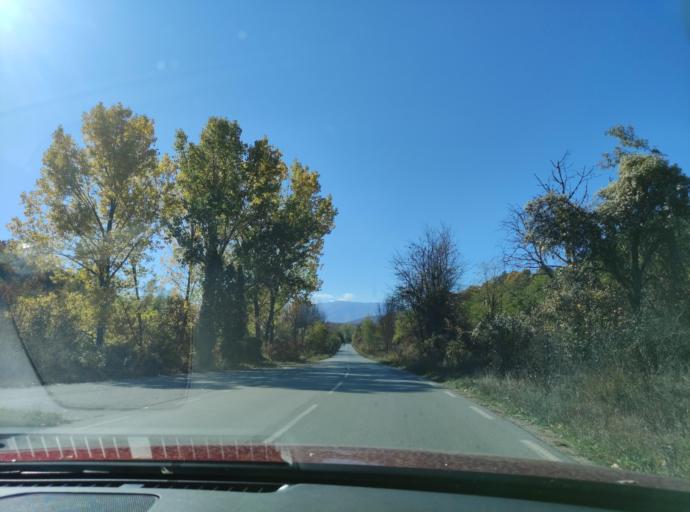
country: BG
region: Montana
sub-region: Obshtina Montana
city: Montana
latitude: 43.3999
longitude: 23.1299
